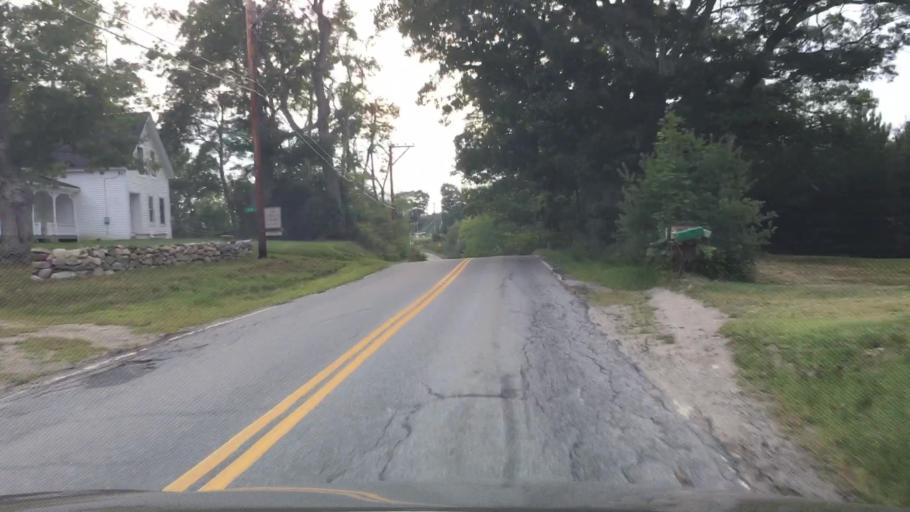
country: US
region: Maine
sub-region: Hancock County
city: Penobscot
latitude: 44.4718
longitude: -68.7352
